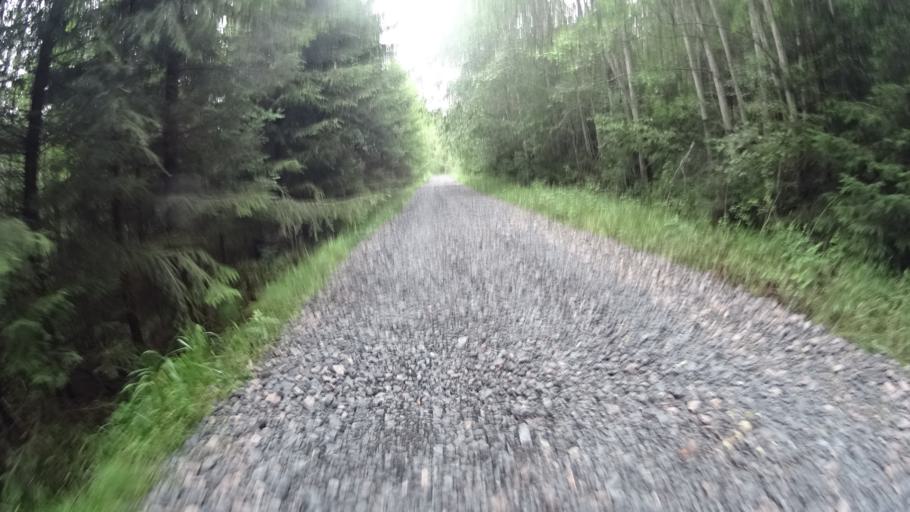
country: FI
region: Uusimaa
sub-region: Helsinki
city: Karkkila
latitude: 60.5867
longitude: 24.1541
